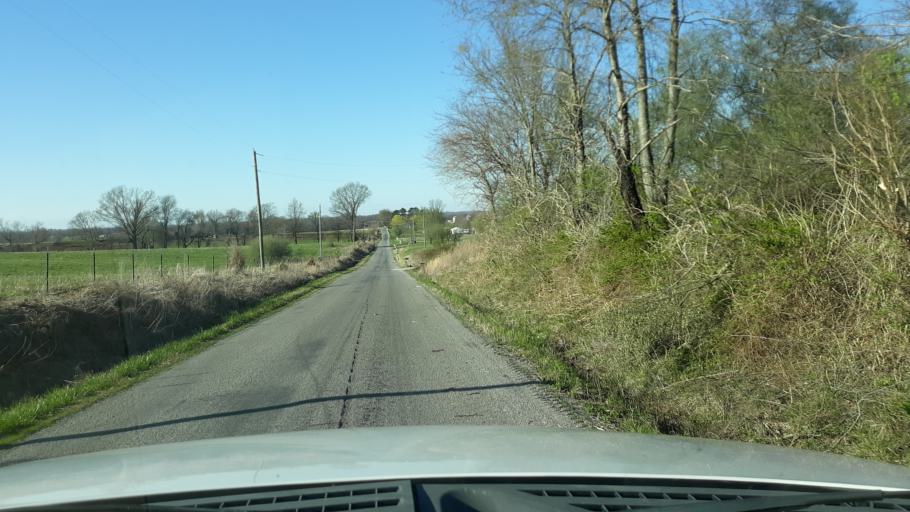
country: US
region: Illinois
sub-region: Saline County
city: Harrisburg
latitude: 37.7767
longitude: -88.6013
